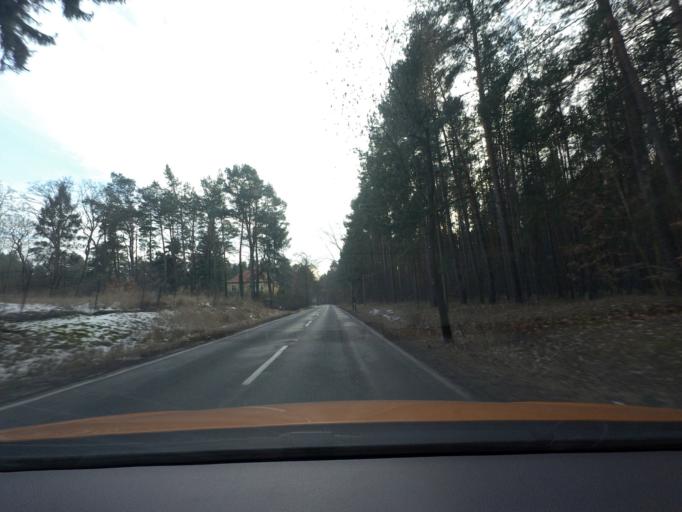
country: DE
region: Brandenburg
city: Wandlitz
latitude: 52.7371
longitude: 13.3688
